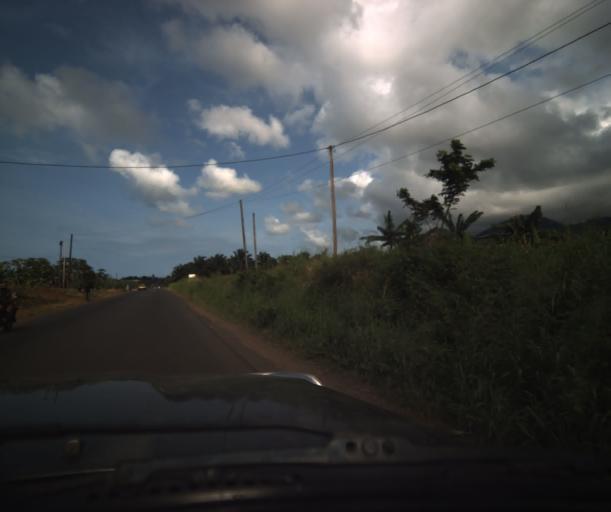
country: CM
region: South-West Province
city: Limbe
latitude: 4.0151
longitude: 9.1628
